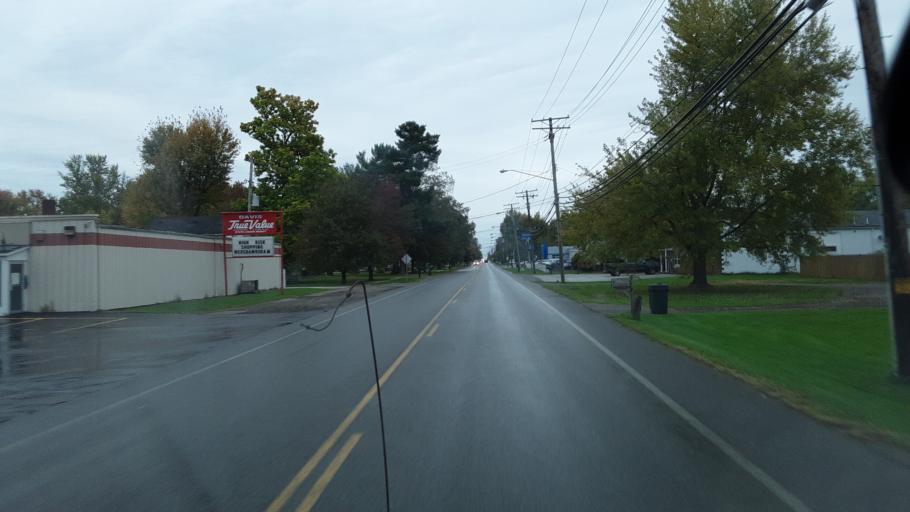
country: US
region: Ohio
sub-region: Ashtabula County
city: Orwell
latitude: 41.5353
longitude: -80.8582
